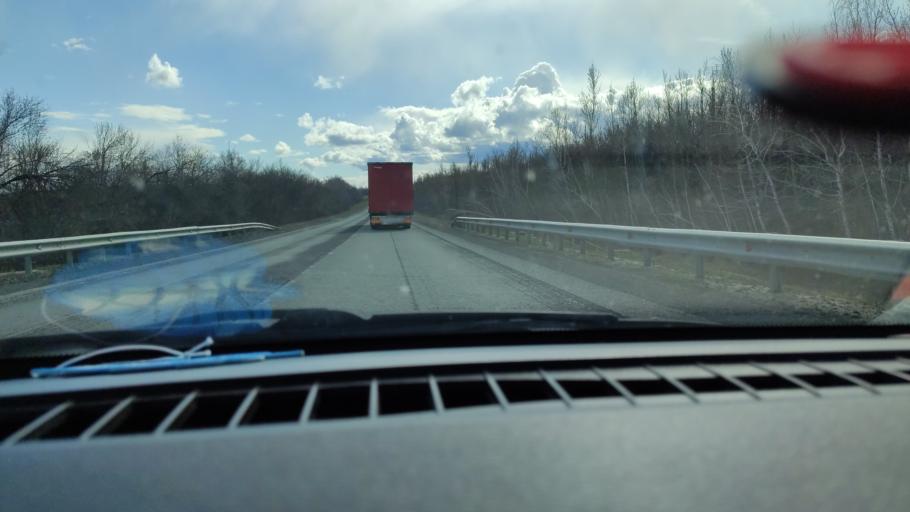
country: RU
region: Saratov
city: Dukhovnitskoye
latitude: 52.6273
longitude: 48.1811
